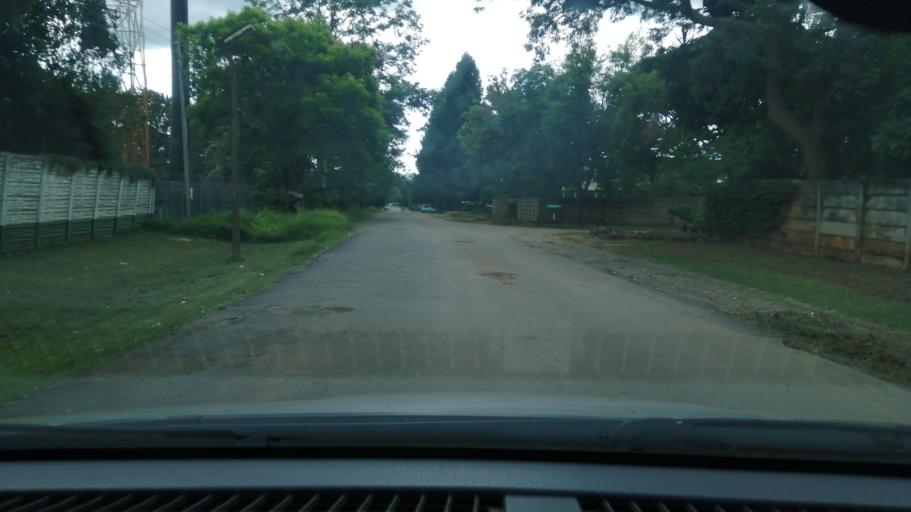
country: ZW
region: Harare
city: Harare
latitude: -17.7734
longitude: 31.0994
